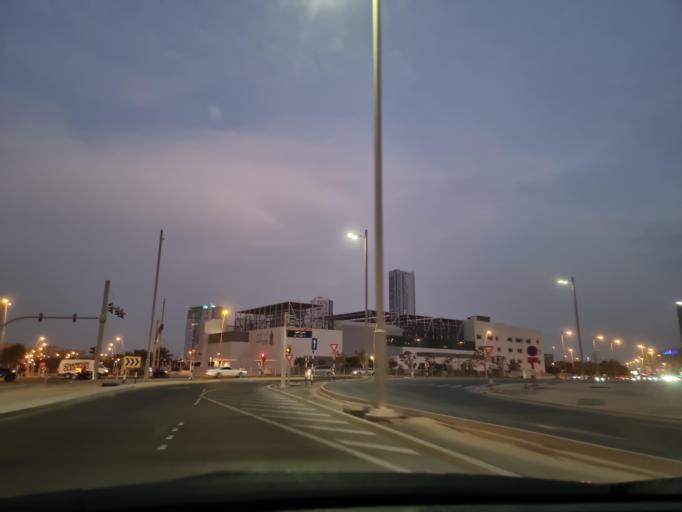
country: AE
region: Abu Dhabi
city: Abu Dhabi
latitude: 24.4950
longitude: 54.4059
